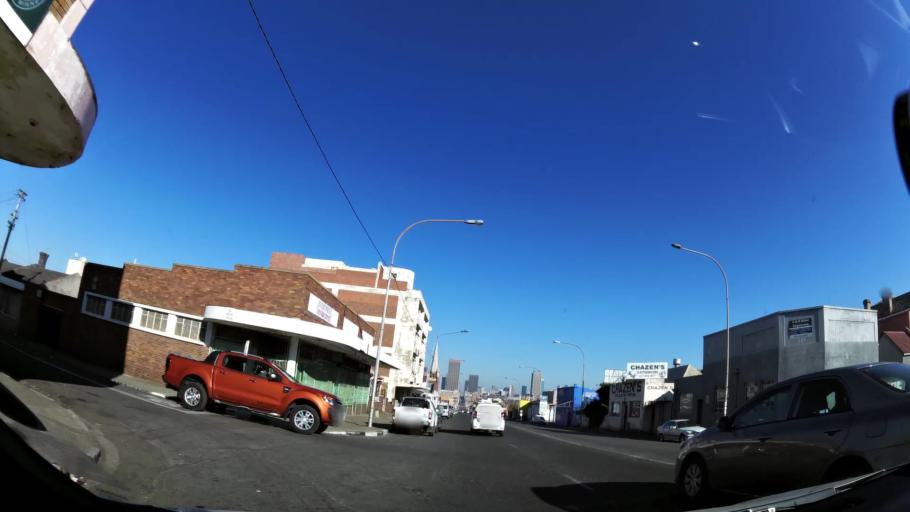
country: ZA
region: Gauteng
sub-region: City of Johannesburg Metropolitan Municipality
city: Johannesburg
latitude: -26.2024
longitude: 28.0694
